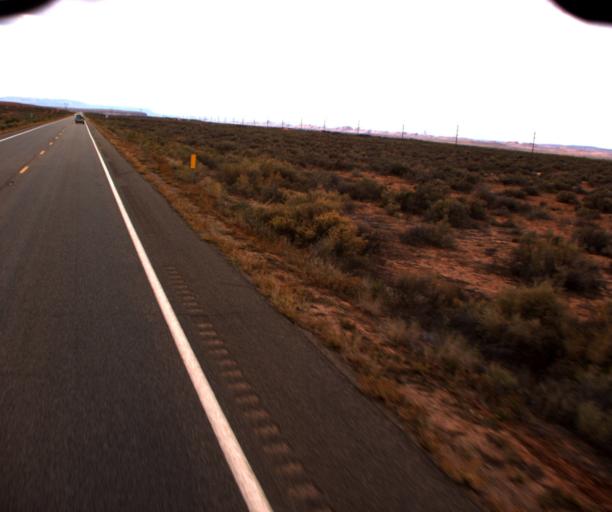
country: US
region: Arizona
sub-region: Navajo County
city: Kayenta
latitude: 36.8091
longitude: -109.9043
